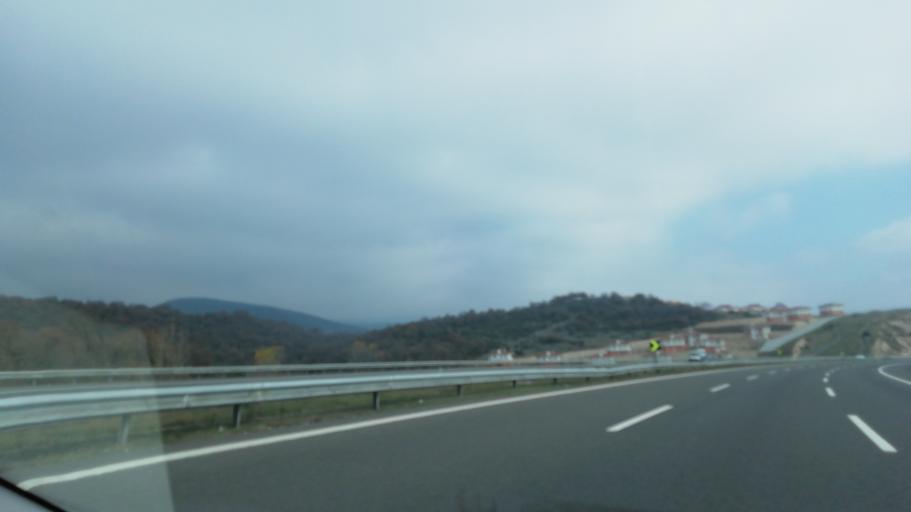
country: TR
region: Bolu
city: Bolu
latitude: 40.7401
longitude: 31.5405
